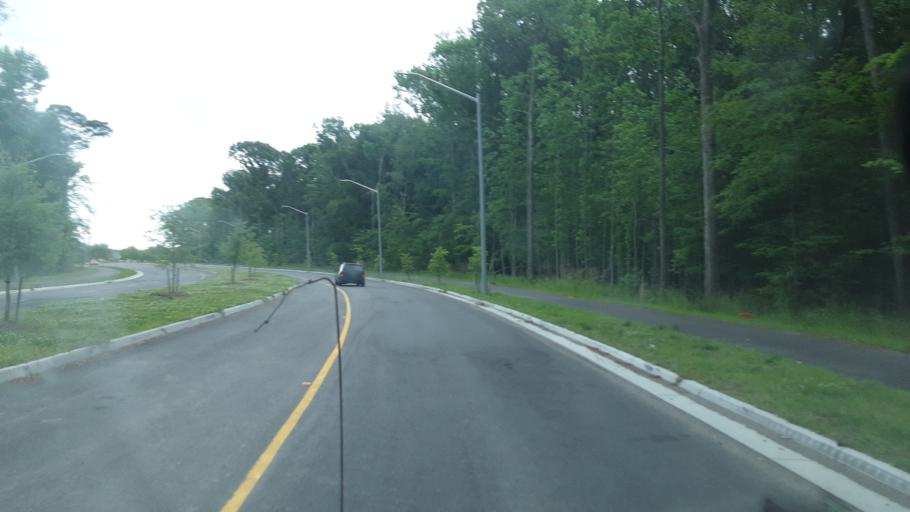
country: US
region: Virginia
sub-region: City of Virginia Beach
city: Virginia Beach
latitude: 36.7595
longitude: -76.0181
